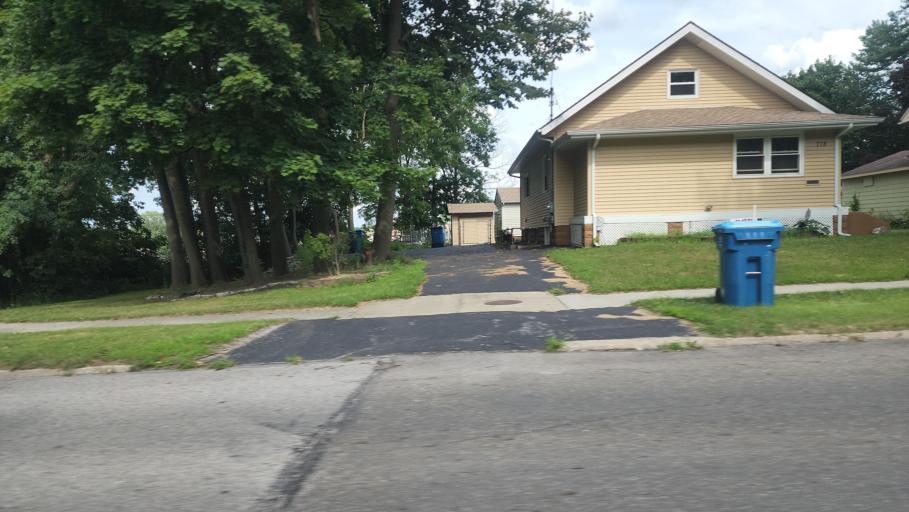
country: US
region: Ohio
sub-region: Mahoning County
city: Struthers
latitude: 41.0520
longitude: -80.6036
